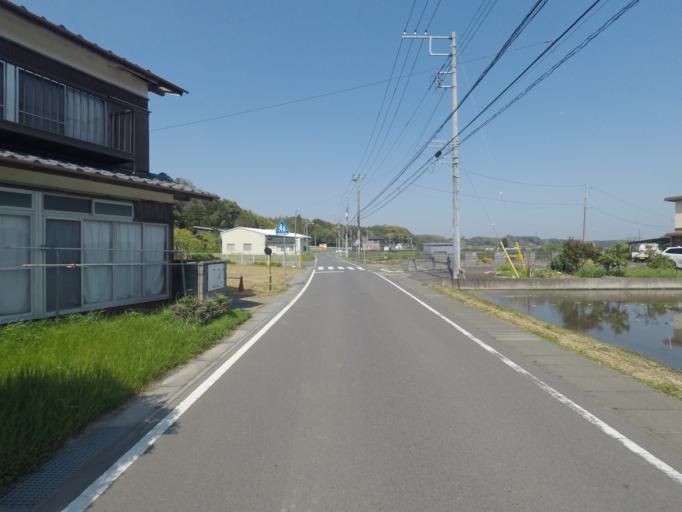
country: JP
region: Ibaraki
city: Ami
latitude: 36.0721
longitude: 140.2540
